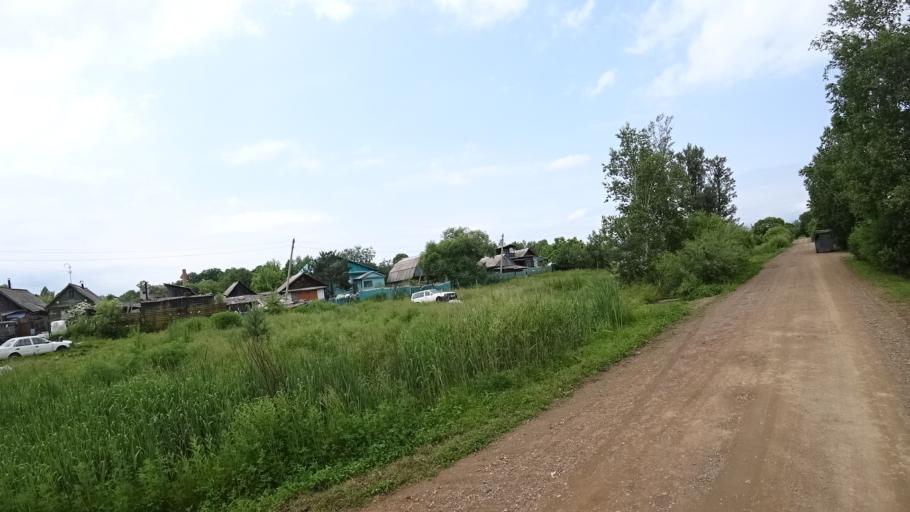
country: RU
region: Primorskiy
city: Novosysoyevka
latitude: 44.2279
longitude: 133.3673
